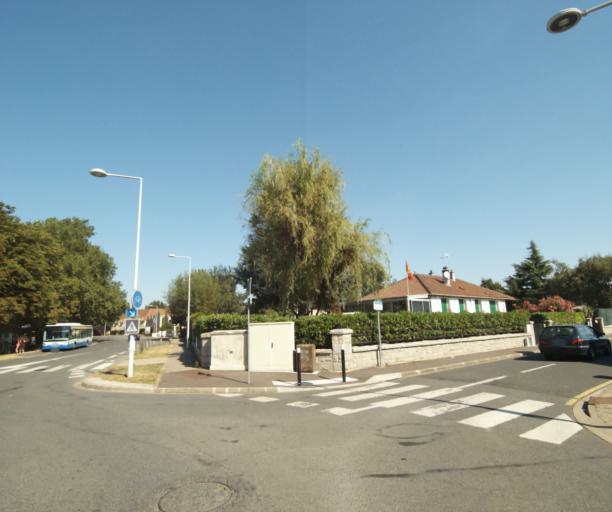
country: FR
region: Ile-de-France
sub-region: Departement de Seine-et-Marne
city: Moissy-Cramayel
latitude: 48.6235
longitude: 2.5991
